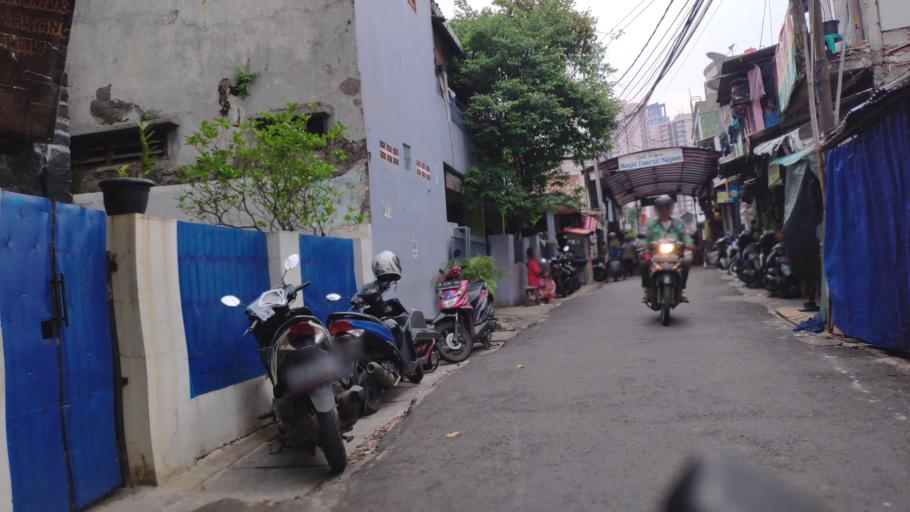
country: ID
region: Jakarta Raya
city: Jakarta
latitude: -6.2179
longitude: 106.8409
